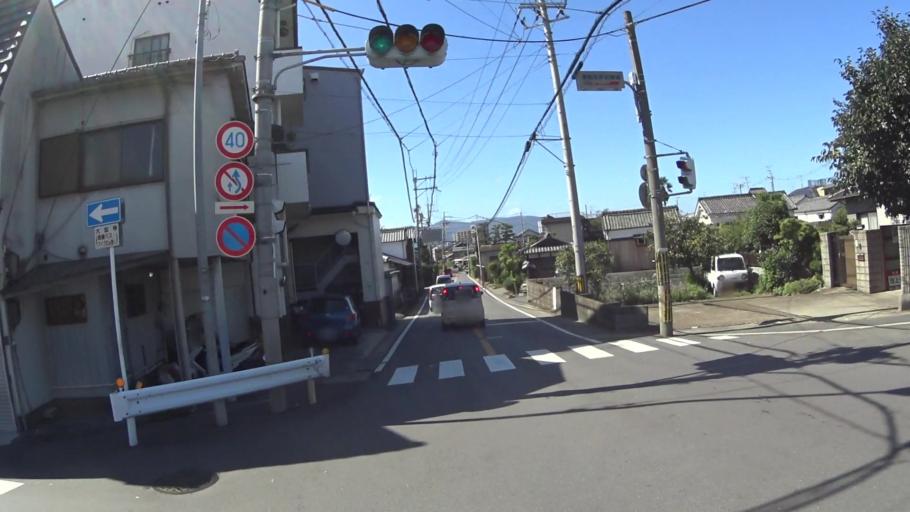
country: JP
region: Kyoto
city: Muko
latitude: 34.9455
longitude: 135.7336
